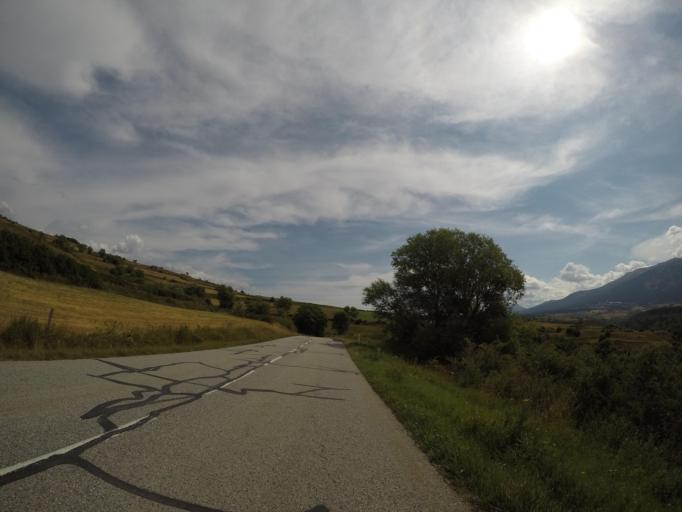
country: ES
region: Catalonia
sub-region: Provincia de Girona
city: Llivia
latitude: 42.4883
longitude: 2.0502
